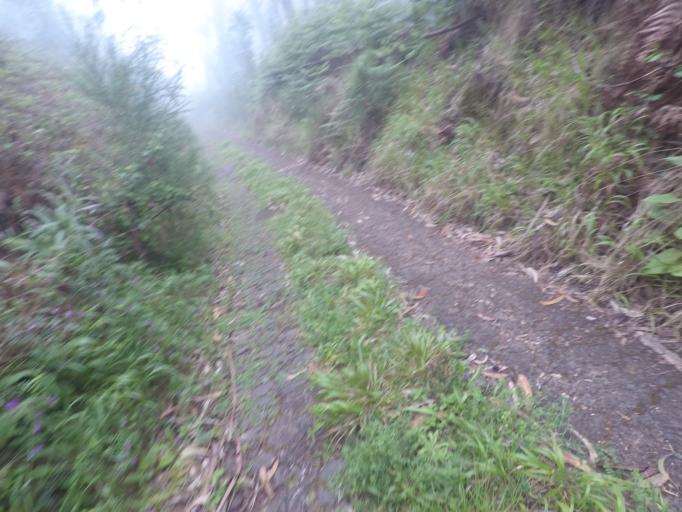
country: PT
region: Madeira
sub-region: Calheta
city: Arco da Calheta
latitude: 32.7262
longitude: -17.0945
